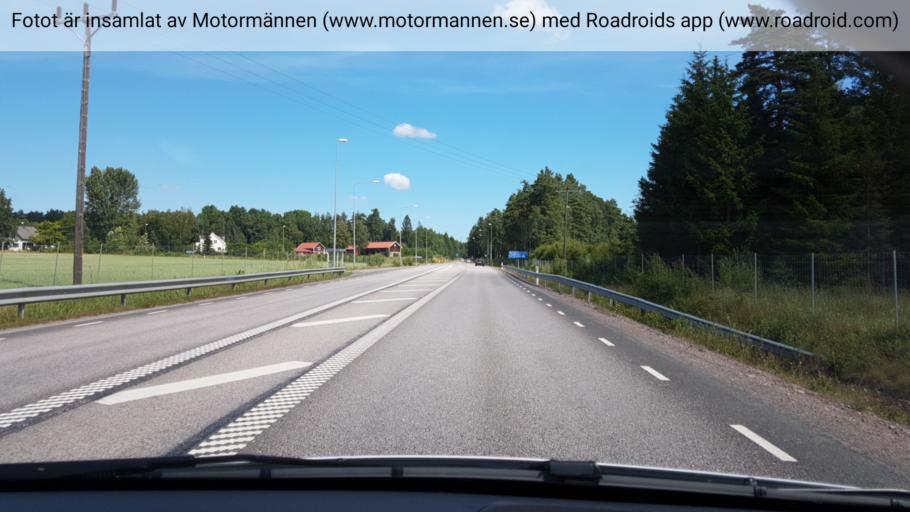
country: SE
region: Vaestra Goetaland
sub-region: Tibro Kommun
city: Tibro
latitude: 58.4434
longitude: 14.1844
